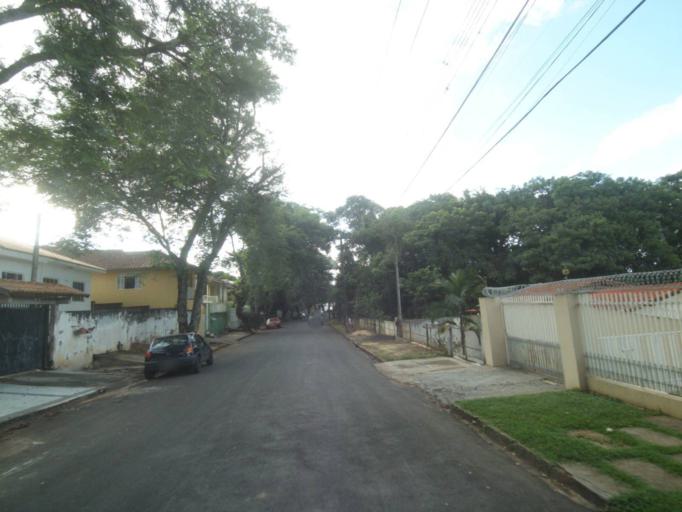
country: BR
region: Parana
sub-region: Telemaco Borba
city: Telemaco Borba
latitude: -24.3291
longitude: -50.6125
